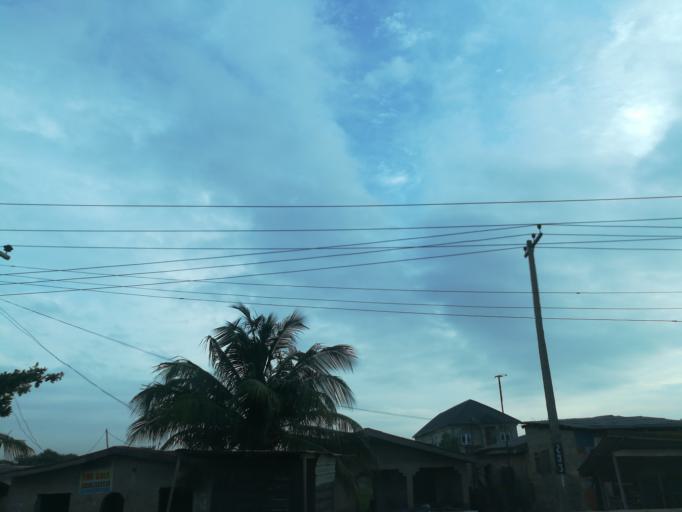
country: NG
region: Lagos
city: Ebute Ikorodu
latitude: 6.6130
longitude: 3.4797
